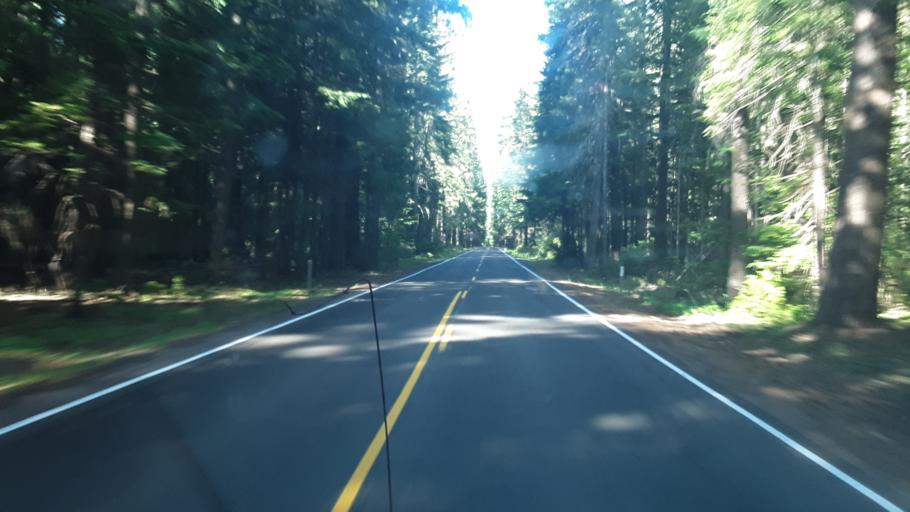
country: US
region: Oregon
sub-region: Jackson County
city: Shady Cove
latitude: 42.9468
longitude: -122.4126
